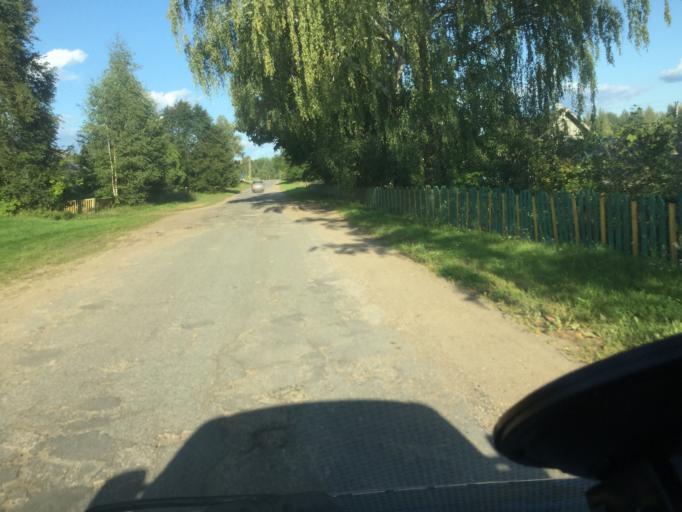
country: BY
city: Osveya
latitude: 56.0207
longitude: 28.2628
